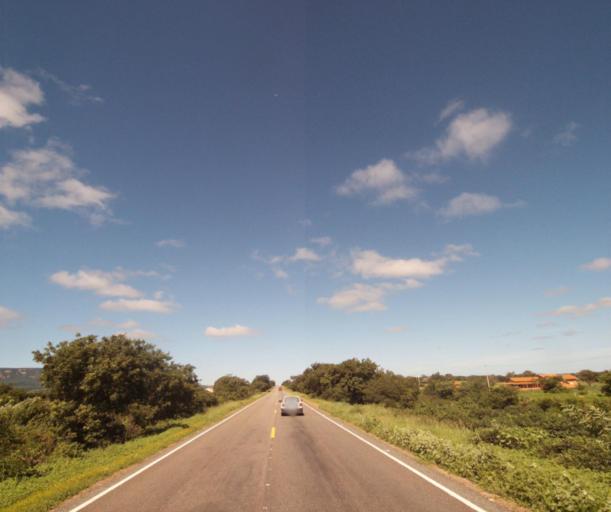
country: BR
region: Bahia
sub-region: Palmas De Monte Alto
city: Palmas de Monte Alto
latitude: -14.2410
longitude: -43.0564
